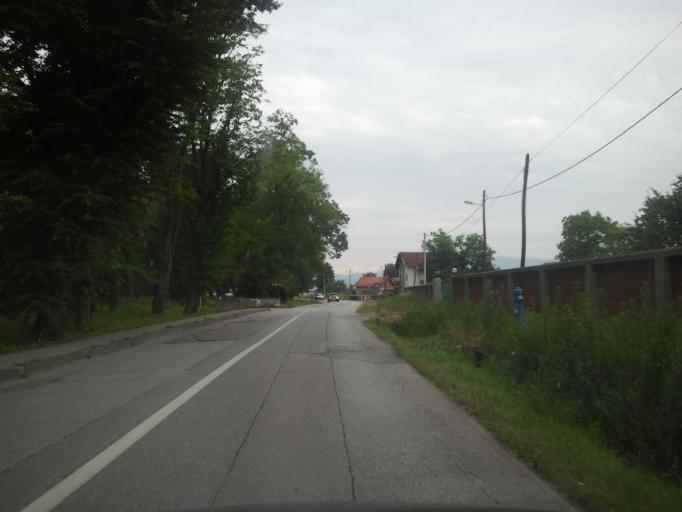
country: HR
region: Grad Zagreb
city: Zadvorsko
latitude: 45.7291
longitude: 15.9108
